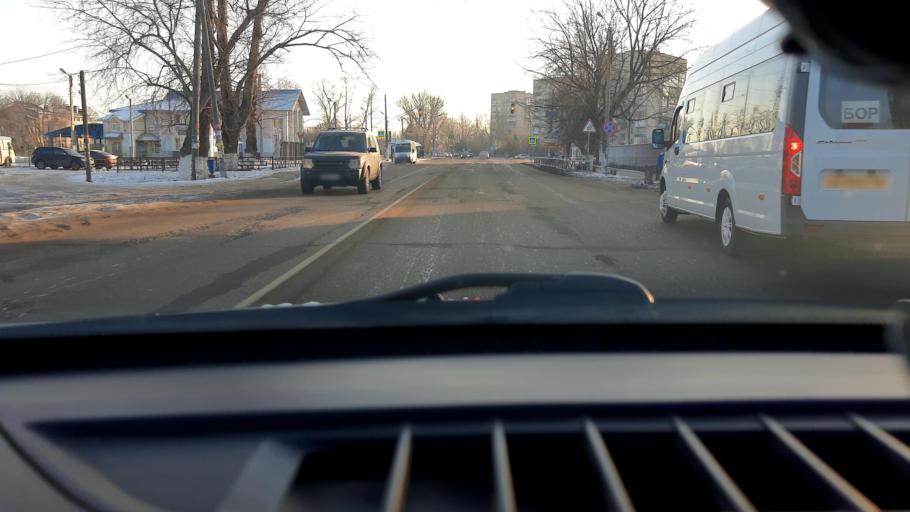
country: RU
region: Nizjnij Novgorod
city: Bor
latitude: 56.3567
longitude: 44.0723
